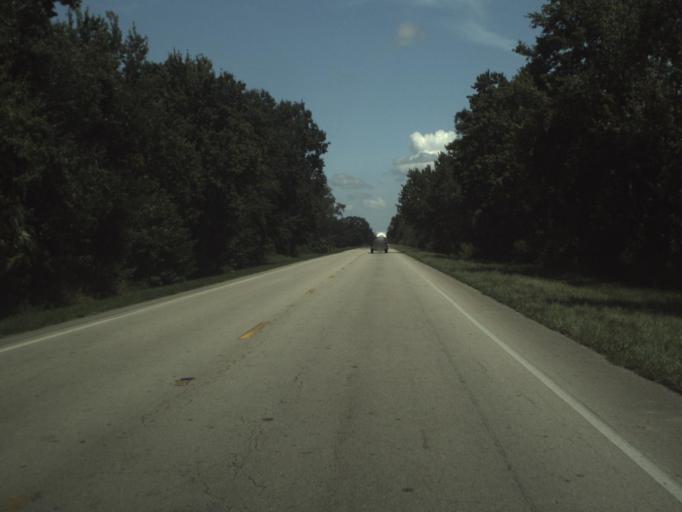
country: US
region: Florida
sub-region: Martin County
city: Indiantown
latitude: 27.0032
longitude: -80.4419
